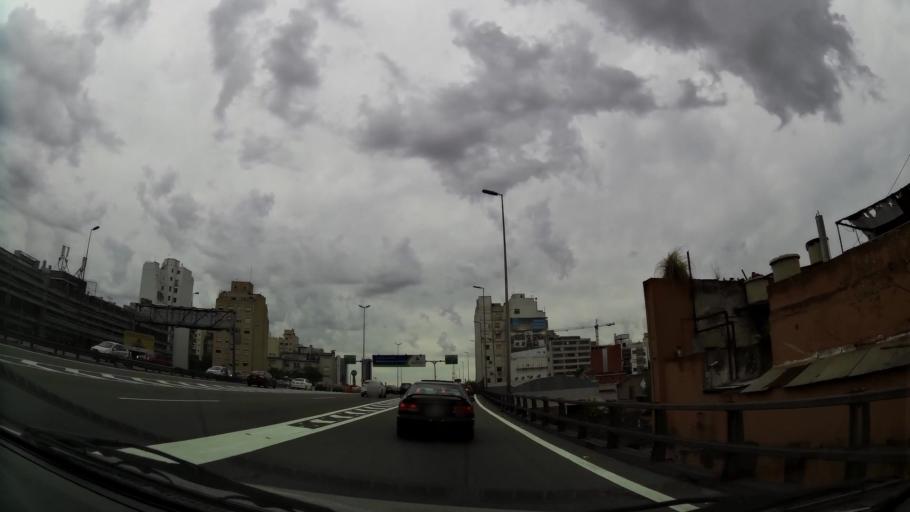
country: AR
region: Buenos Aires F.D.
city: Buenos Aires
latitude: -34.6227
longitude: -58.3712
